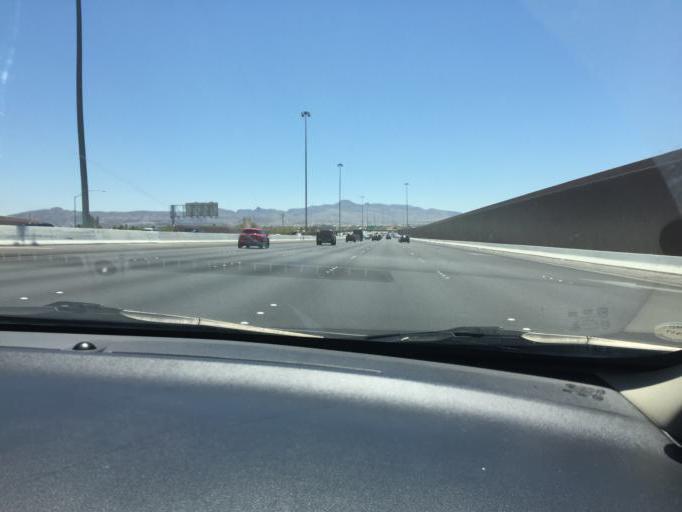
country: US
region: Nevada
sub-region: Clark County
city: Paradise
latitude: 36.0569
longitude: -115.1403
